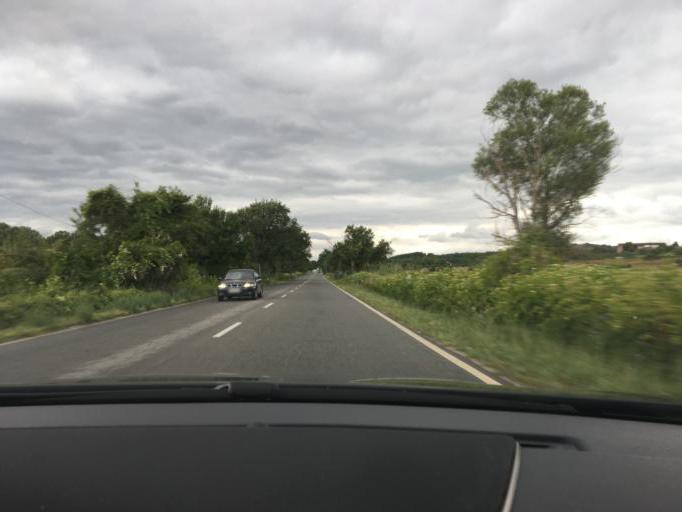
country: BG
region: Kyustendil
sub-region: Obshtina Boboshevo
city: Boboshevo
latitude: 42.2571
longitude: 22.8673
